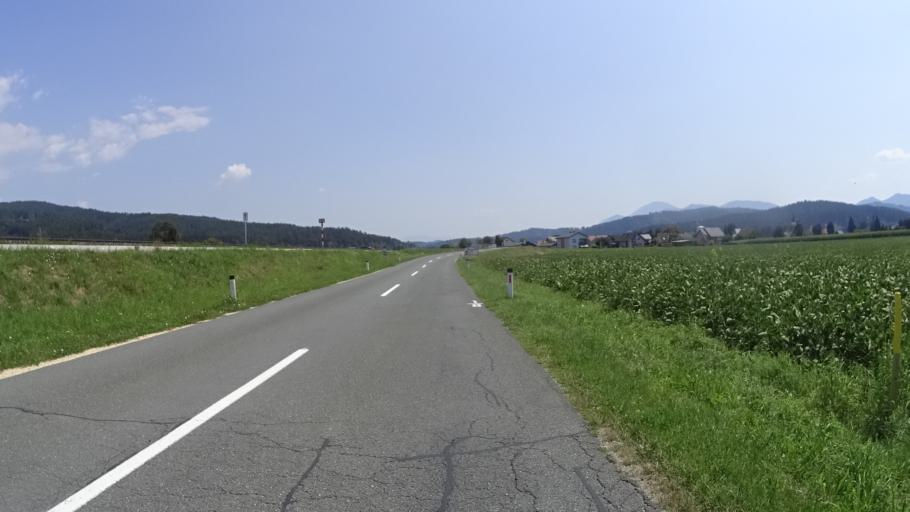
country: AT
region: Carinthia
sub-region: Politischer Bezirk Volkermarkt
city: Bleiburg/Pliberk
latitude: 46.5716
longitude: 14.8010
